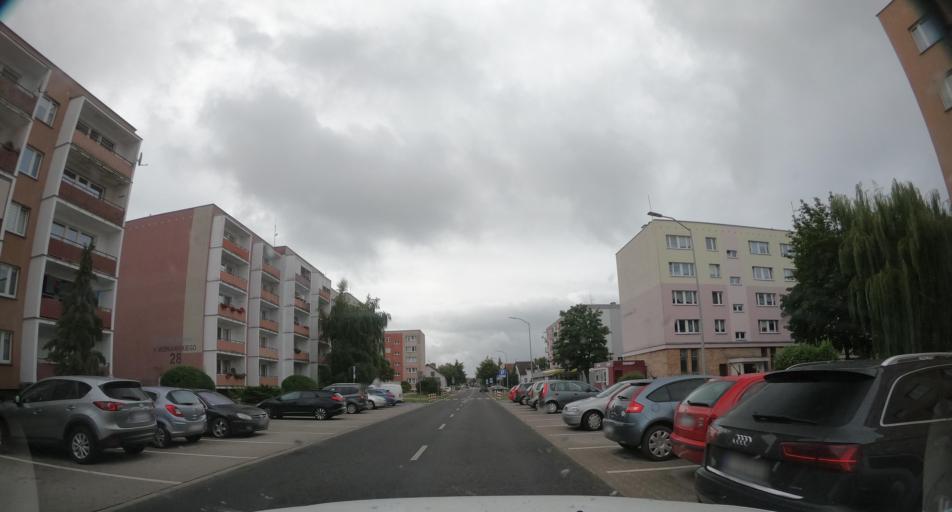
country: PL
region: West Pomeranian Voivodeship
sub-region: Powiat stargardzki
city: Stargard Szczecinski
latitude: 53.3459
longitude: 15.0082
